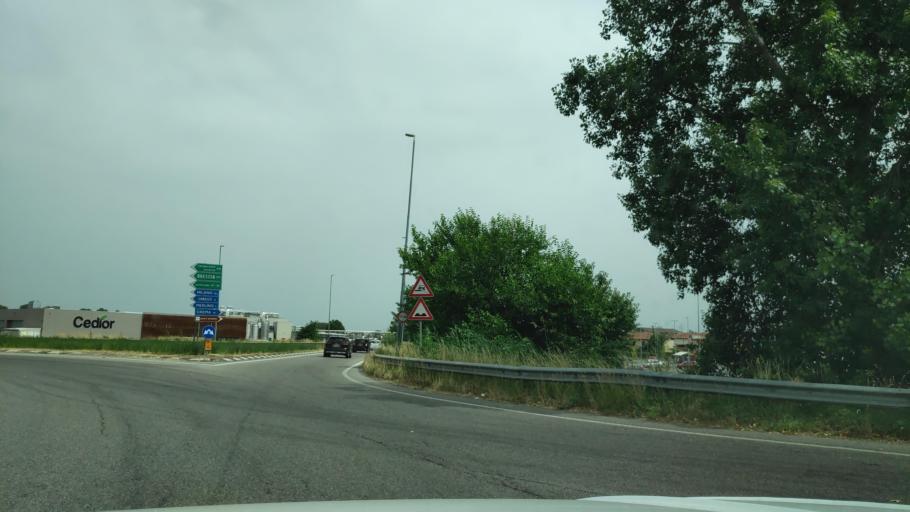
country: IT
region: Lombardy
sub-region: Provincia di Lodi
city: Zelo Buon Persico
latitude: 45.4184
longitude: 9.4269
